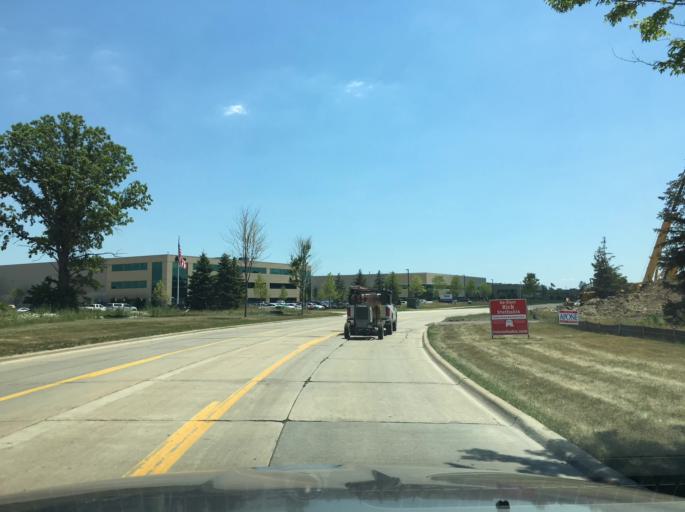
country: US
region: Michigan
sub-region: Macomb County
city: Shelby
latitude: 42.6820
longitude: -83.0130
